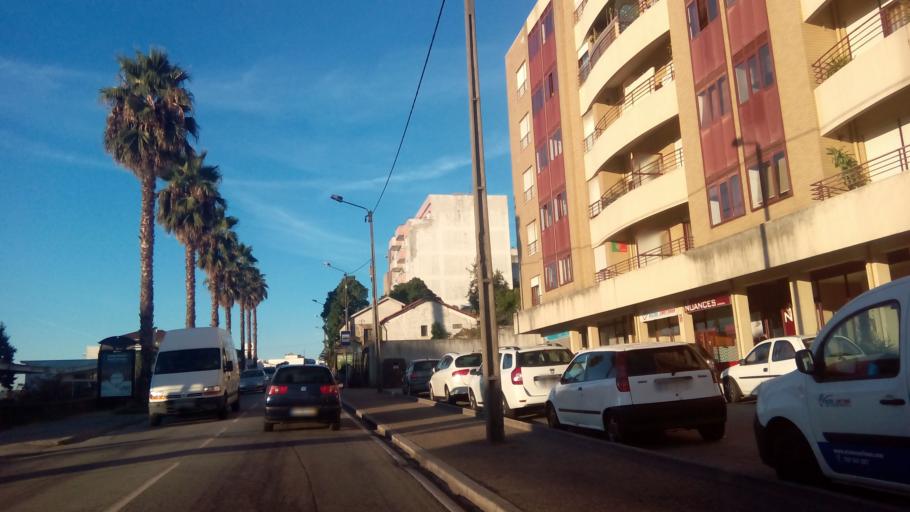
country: PT
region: Porto
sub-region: Paredes
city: Casteloes de Cepeda
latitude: 41.2031
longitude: -8.3409
